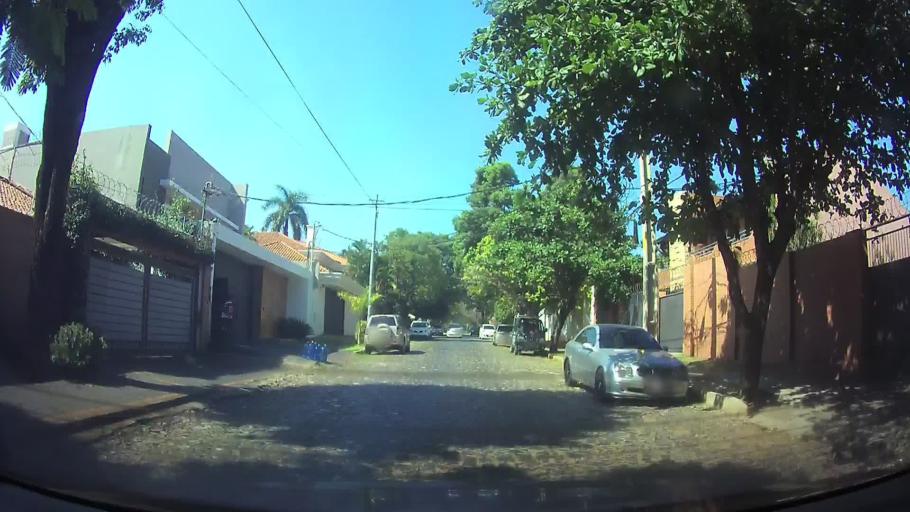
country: PY
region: Central
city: Fernando de la Mora
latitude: -25.2892
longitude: -57.5633
